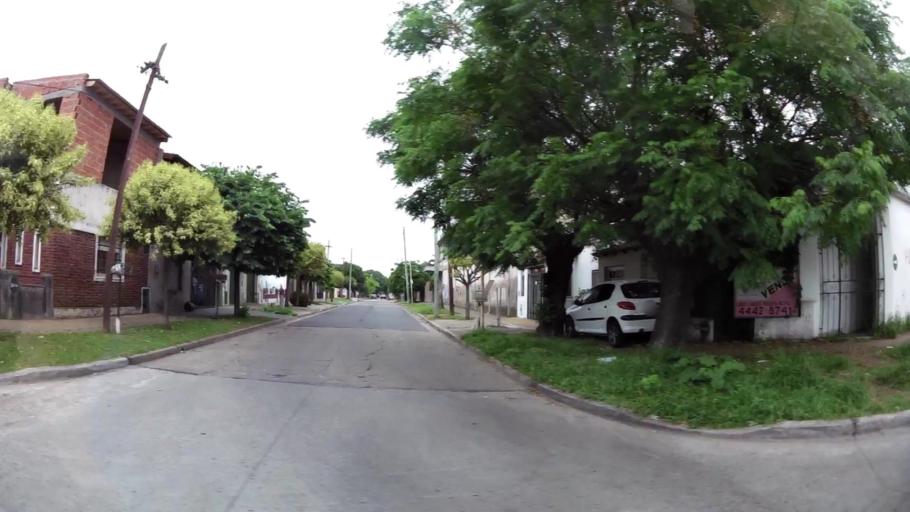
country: AR
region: Buenos Aires F.D.
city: Villa Lugano
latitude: -34.7048
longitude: -58.5142
